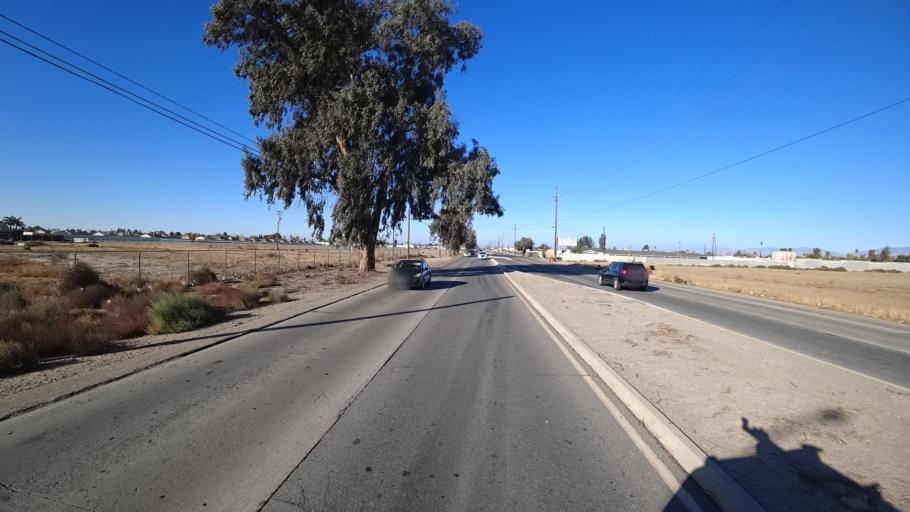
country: US
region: California
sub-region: Kern County
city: Greenfield
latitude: 35.2987
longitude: -119.0031
